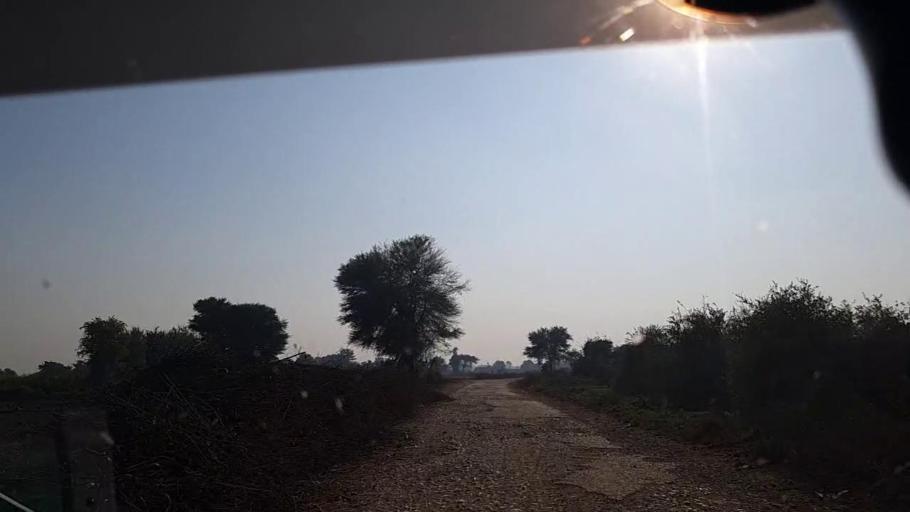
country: PK
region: Sindh
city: Hingorja
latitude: 27.2165
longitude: 68.2652
